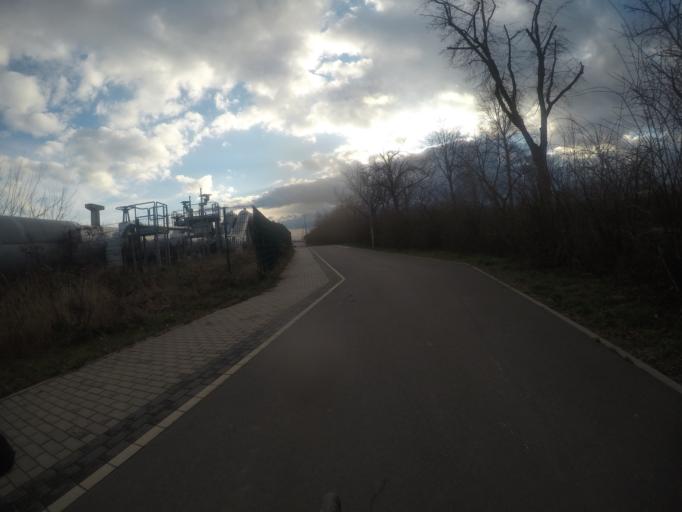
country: DE
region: Berlin
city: Falkenberg
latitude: 52.5638
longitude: 13.5385
